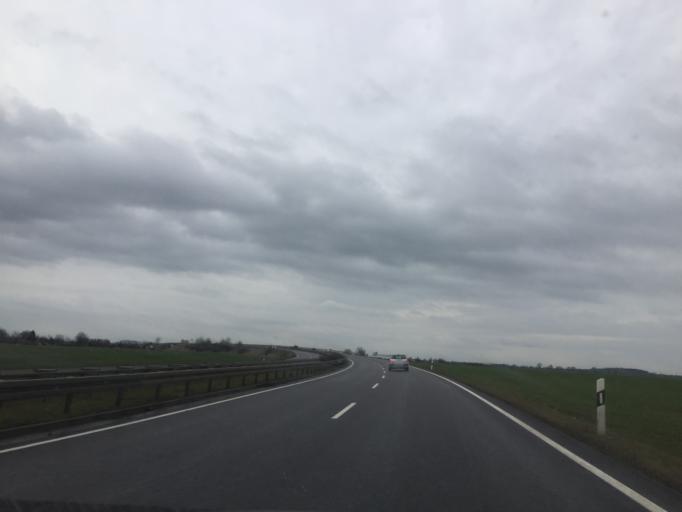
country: DE
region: Saxony-Anhalt
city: Hohendodeleben
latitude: 52.0486
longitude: 11.5221
